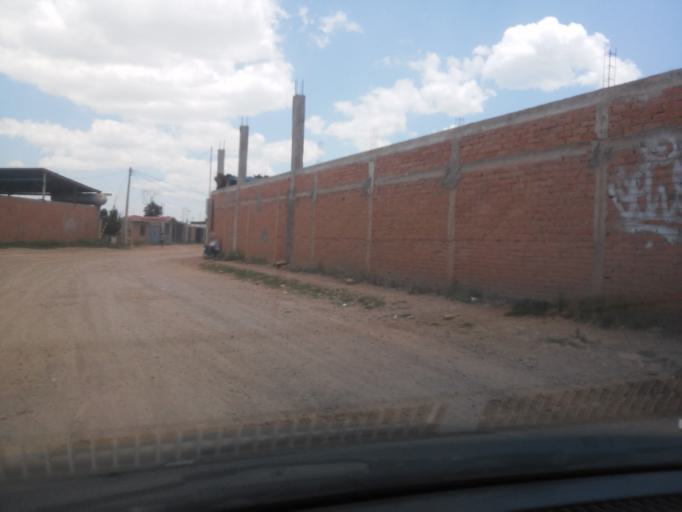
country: MX
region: Durango
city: Victoria de Durango
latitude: 24.0615
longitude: -104.6268
